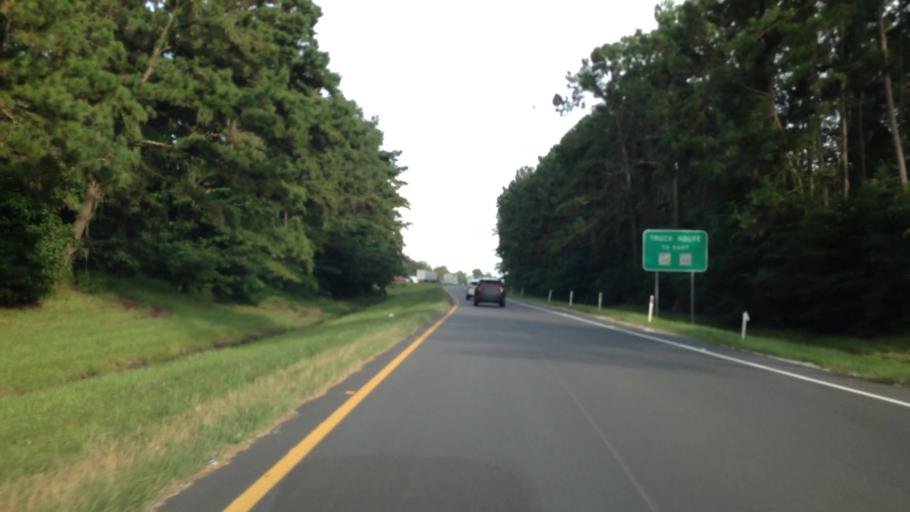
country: US
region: Florida
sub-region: Alachua County
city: Gainesville
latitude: 29.6162
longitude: -82.3864
